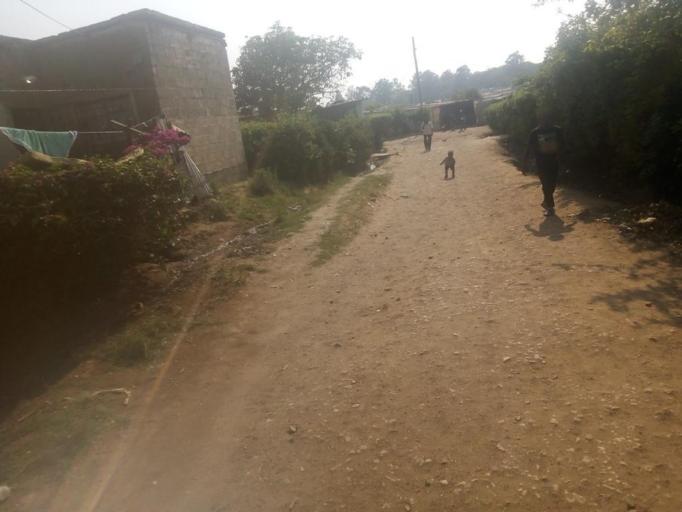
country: ZM
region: Lusaka
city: Lusaka
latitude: -15.4037
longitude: 28.3613
